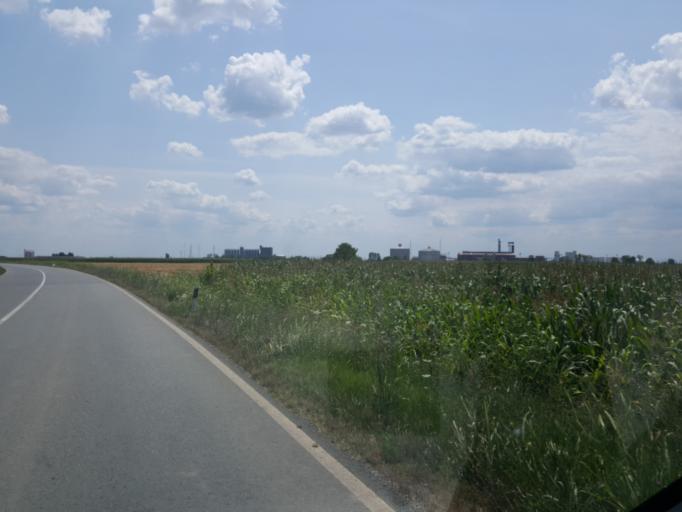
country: RS
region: Autonomna Pokrajina Vojvodina
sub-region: Sremski Okrug
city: Pecinci
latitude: 44.9020
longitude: 19.9568
